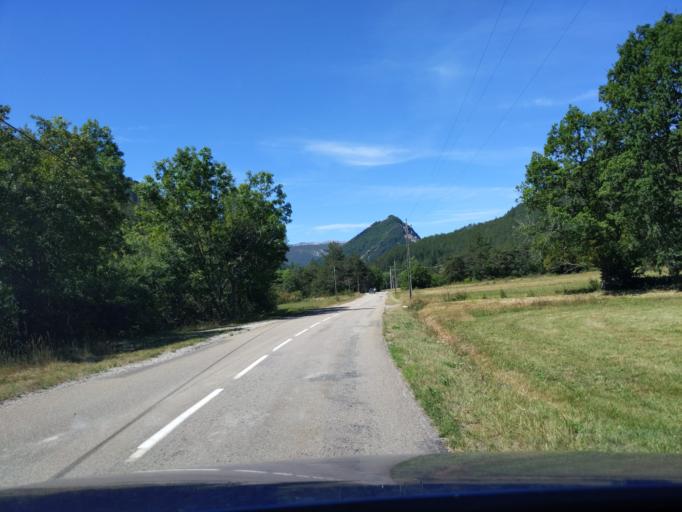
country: FR
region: Rhone-Alpes
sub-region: Departement de la Drome
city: Die
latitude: 44.6175
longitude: 5.5038
